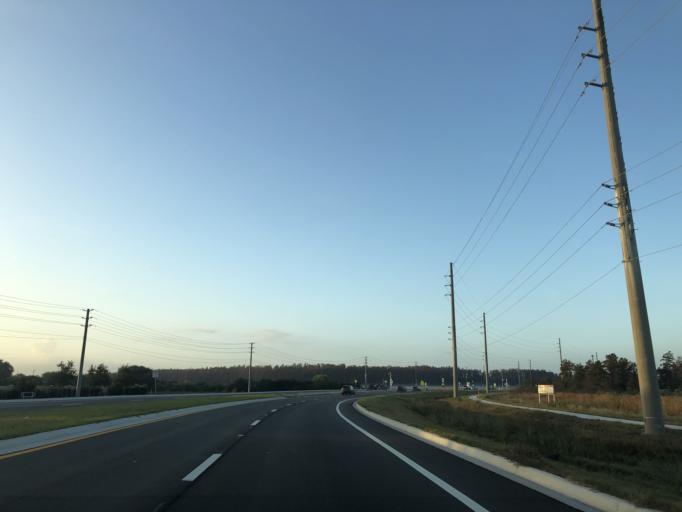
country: US
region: Florida
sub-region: Osceola County
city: Kissimmee
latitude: 28.3214
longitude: -81.4417
